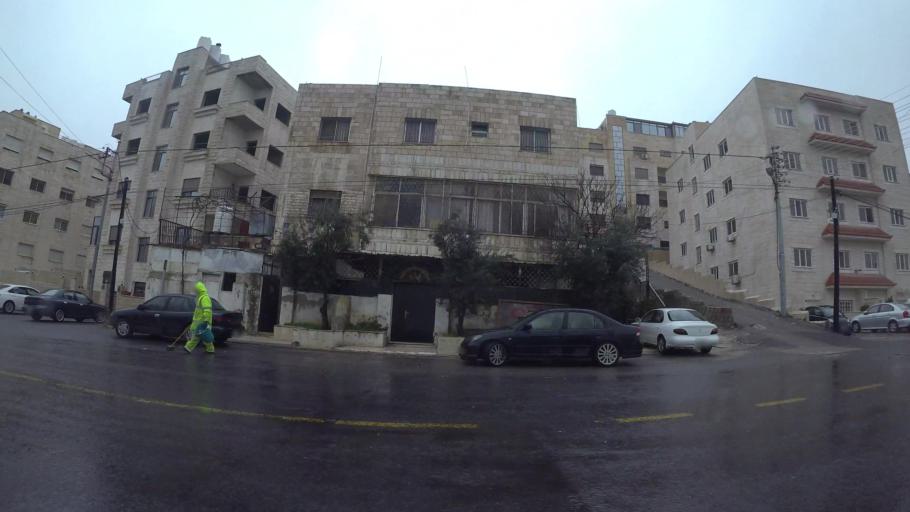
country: JO
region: Amman
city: Al Jubayhah
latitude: 32.0174
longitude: 35.8415
